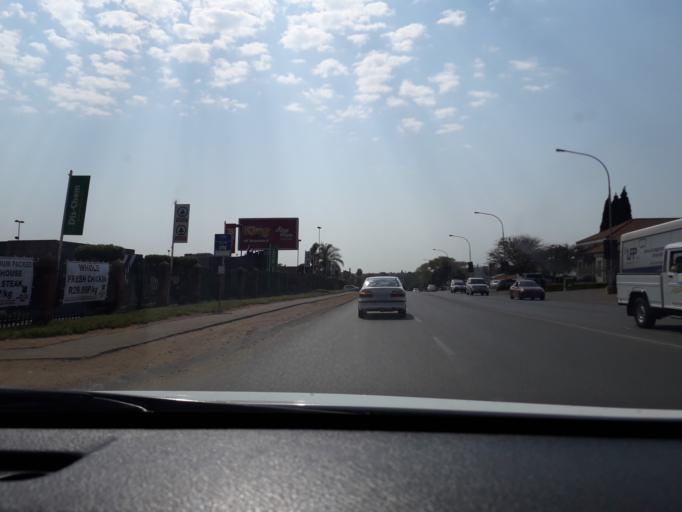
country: ZA
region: Gauteng
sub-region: City of Johannesburg Metropolitan Municipality
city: Modderfontein
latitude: -26.0787
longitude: 28.2482
